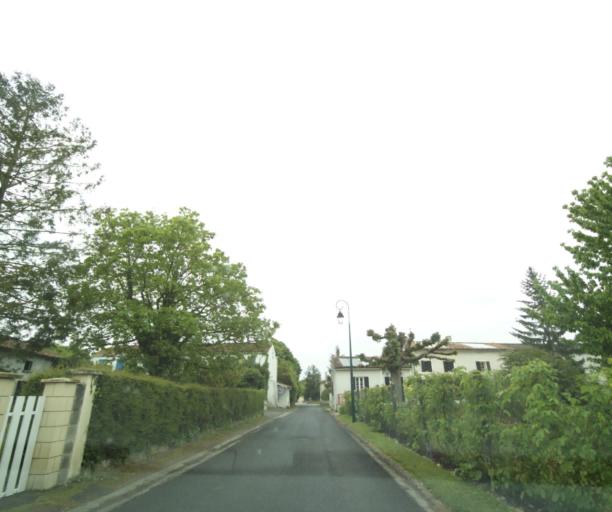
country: FR
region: Poitou-Charentes
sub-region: Departement de la Charente-Maritime
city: Perignac
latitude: 45.6498
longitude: -0.5042
